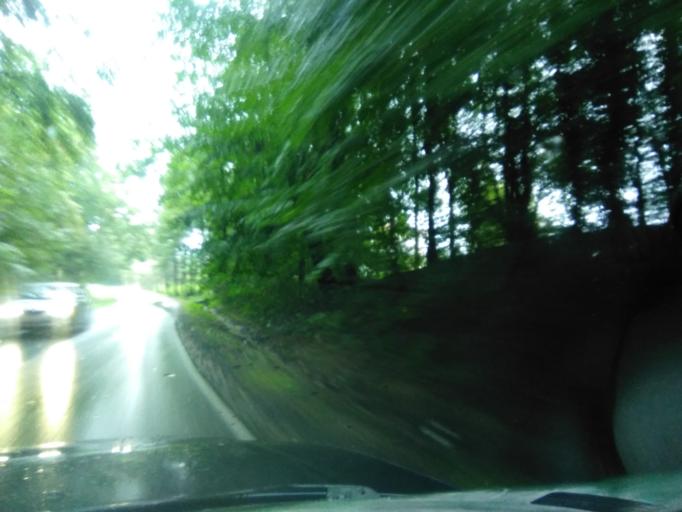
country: PL
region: Subcarpathian Voivodeship
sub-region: Powiat ropczycko-sedziszowski
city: Niedzwiada
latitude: 50.0570
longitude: 21.5357
